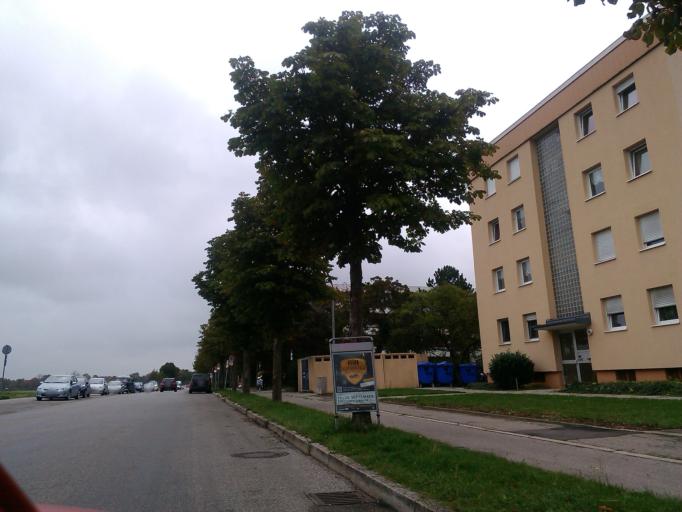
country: DE
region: Bavaria
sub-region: Upper Bavaria
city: Fuerstenfeldbruck
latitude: 48.1812
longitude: 11.2390
